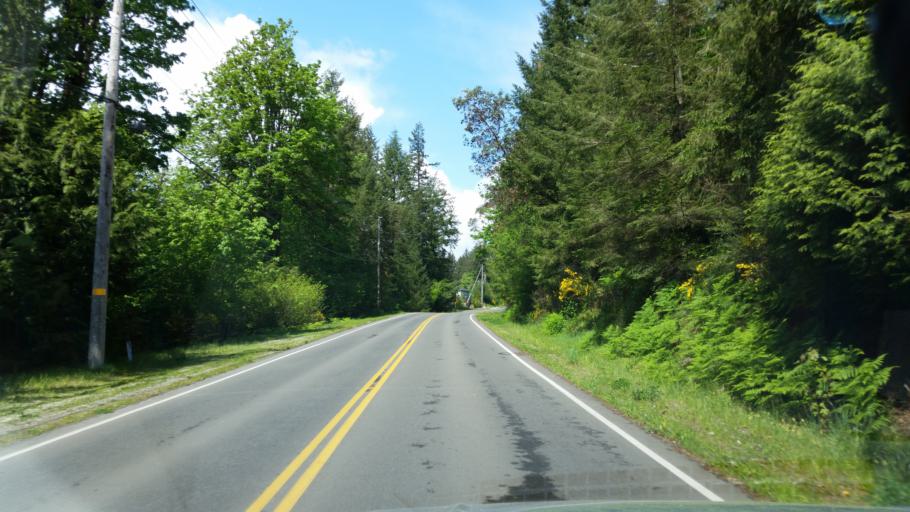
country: US
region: Washington
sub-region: Pierce County
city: Purdy
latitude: 47.3658
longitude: -122.6189
